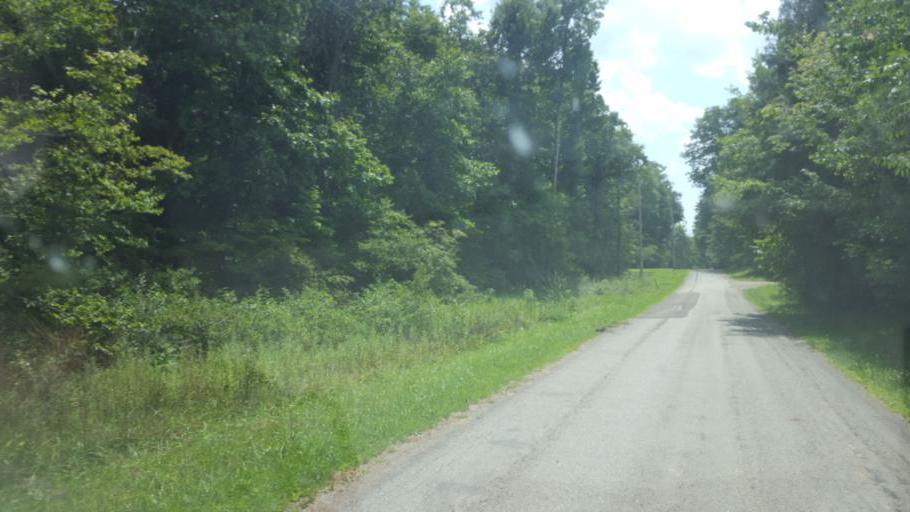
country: US
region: Ohio
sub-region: Knox County
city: Centerburg
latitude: 40.3722
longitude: -82.6336
